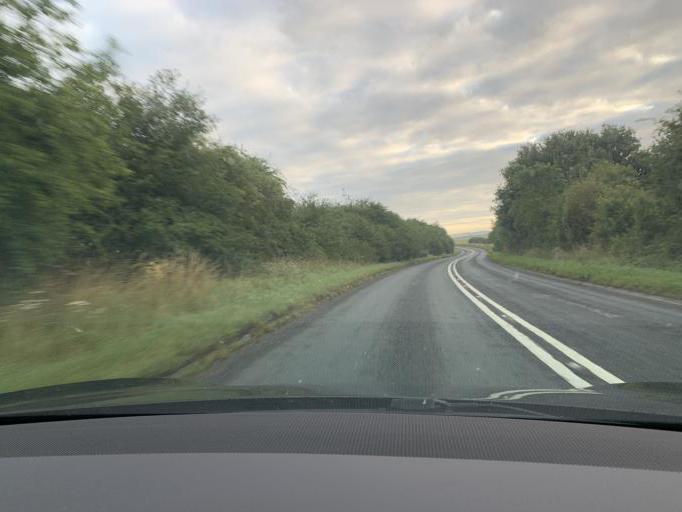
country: GB
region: England
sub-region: Wiltshire
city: Tidworth
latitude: 51.2577
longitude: -1.6673
